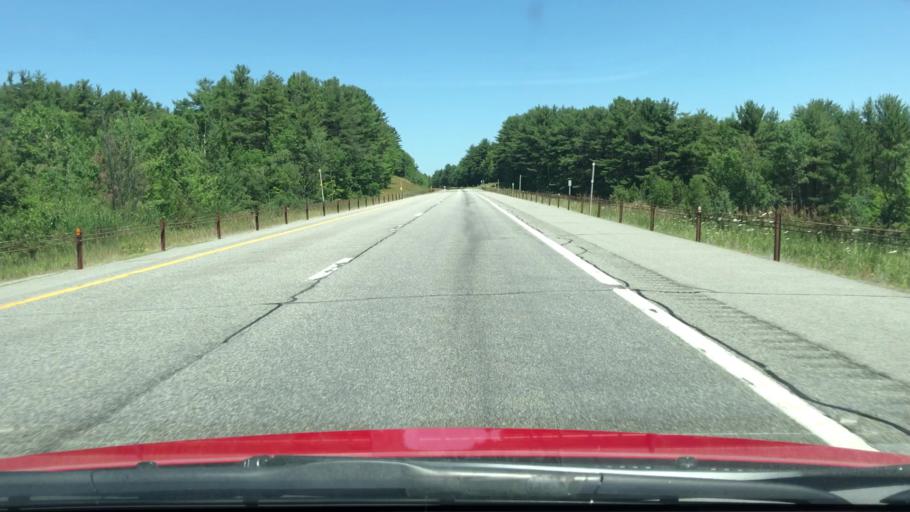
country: US
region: New York
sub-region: Essex County
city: Elizabethtown
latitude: 44.1478
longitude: -73.5832
